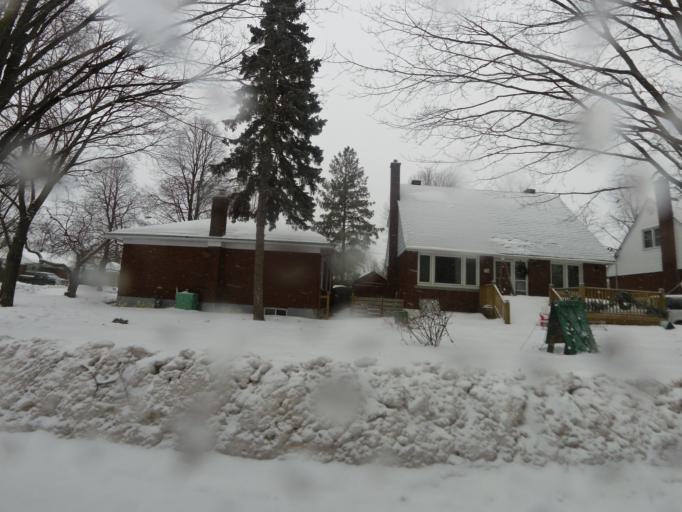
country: CA
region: Ontario
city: Ottawa
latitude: 45.4073
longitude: -75.6398
